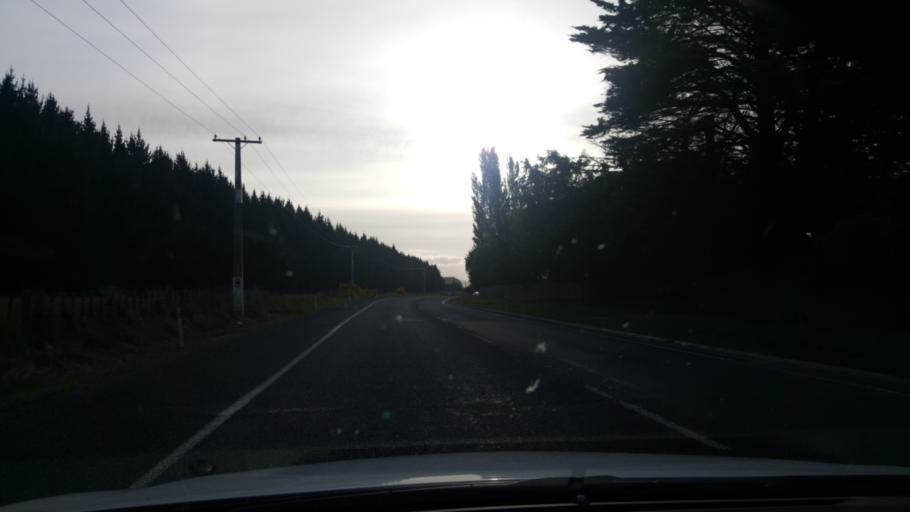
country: NZ
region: Waikato
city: Turangi
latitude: -38.9089
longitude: 175.9134
